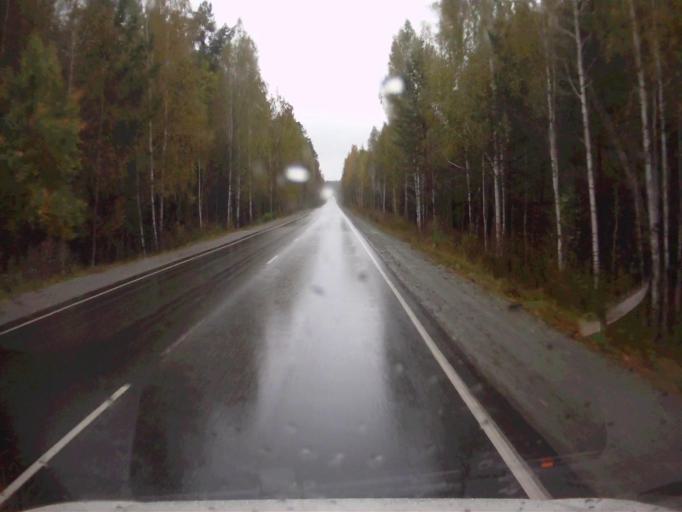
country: RU
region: Chelyabinsk
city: Kyshtym
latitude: 55.6477
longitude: 60.5835
